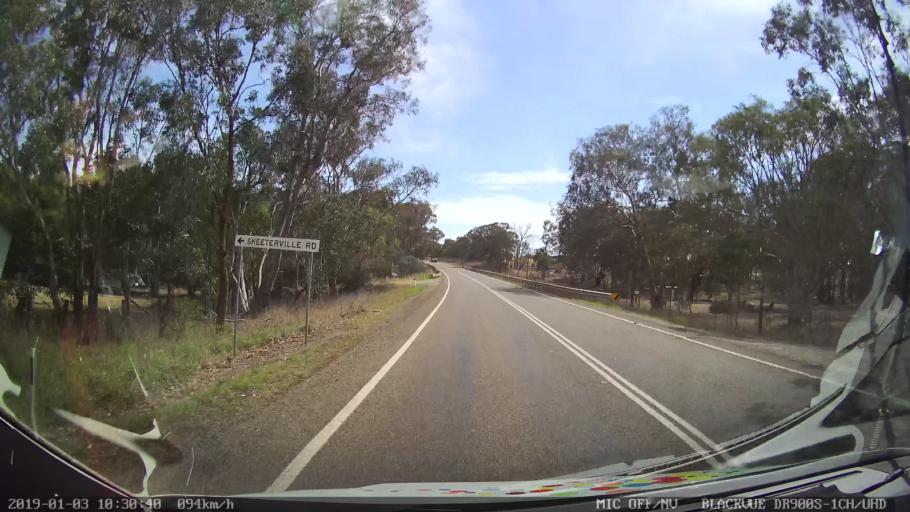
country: AU
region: New South Wales
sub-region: Young
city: Young
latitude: -34.3597
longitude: 148.2707
